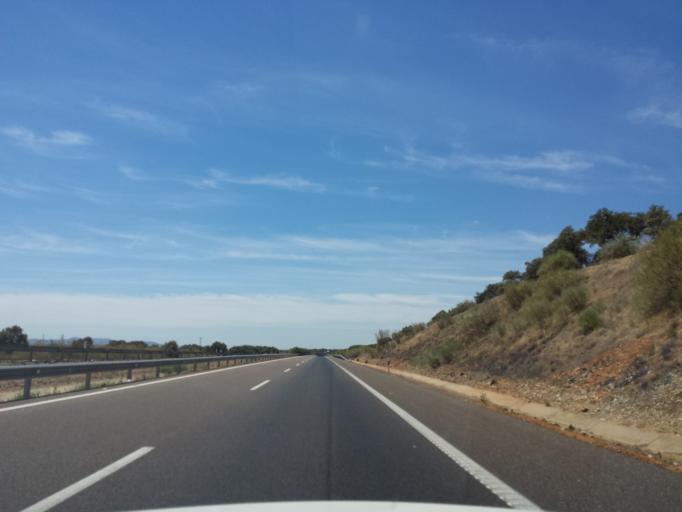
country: ES
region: Extremadura
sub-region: Provincia de Badajoz
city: San Pedro de Merida
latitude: 38.9602
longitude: -6.1585
